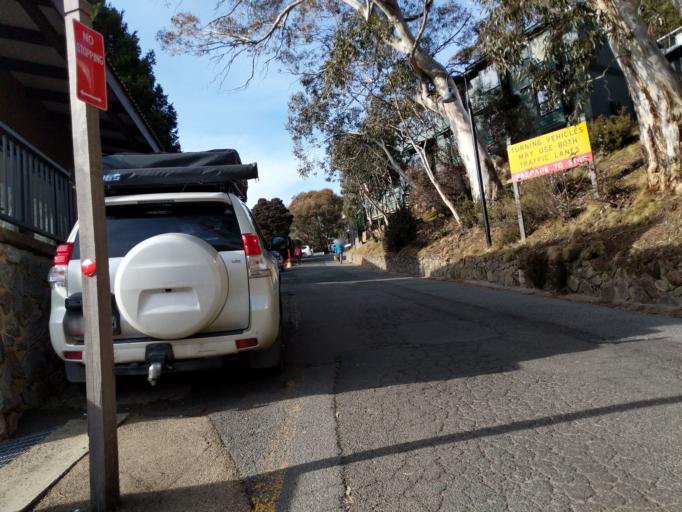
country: AU
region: New South Wales
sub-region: Snowy River
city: Jindabyne
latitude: -36.5047
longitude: 148.3060
